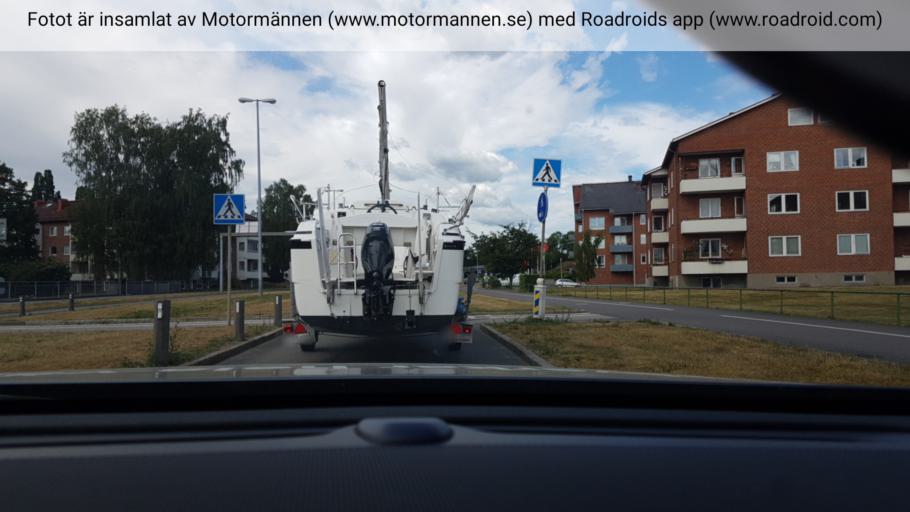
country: SE
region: Skane
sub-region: Hassleholms Kommun
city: Hassleholm
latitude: 56.1565
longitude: 13.7559
